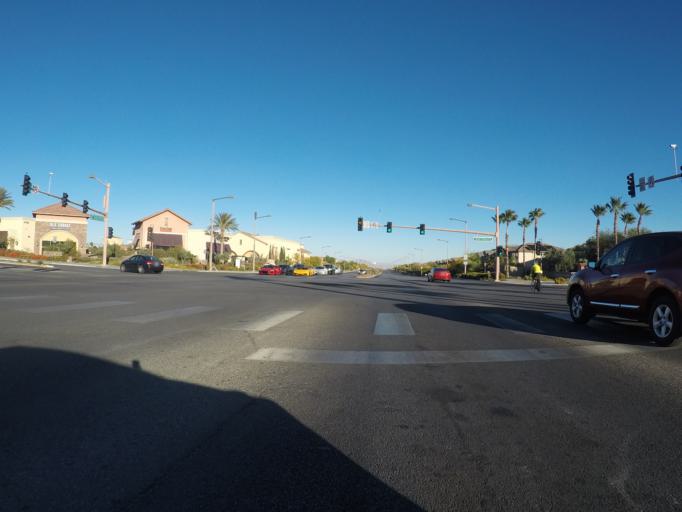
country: US
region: Nevada
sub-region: Clark County
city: Summerlin South
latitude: 36.1589
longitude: -115.3524
